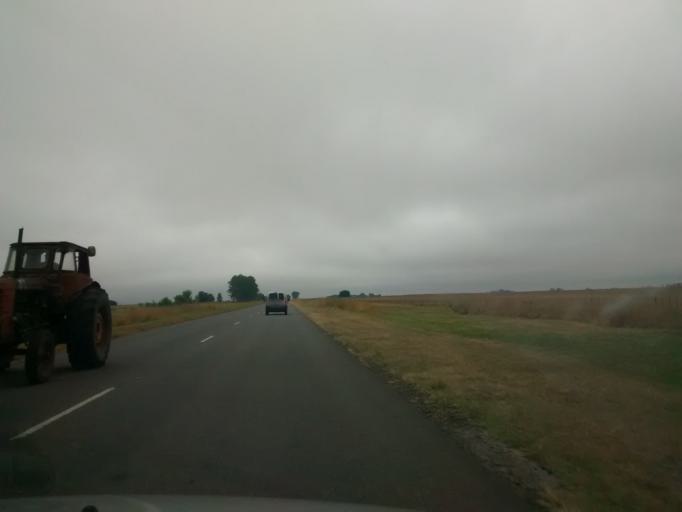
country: AR
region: Buenos Aires
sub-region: Partido de Ayacucho
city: Ayacucho
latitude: -37.2348
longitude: -58.4928
